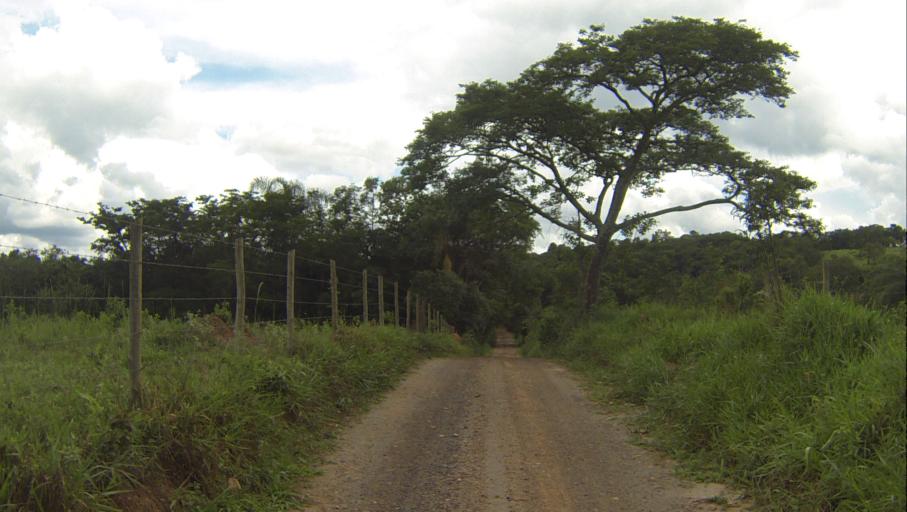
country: BR
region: Minas Gerais
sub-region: Brumadinho
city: Brumadinho
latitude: -20.1649
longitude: -44.1292
